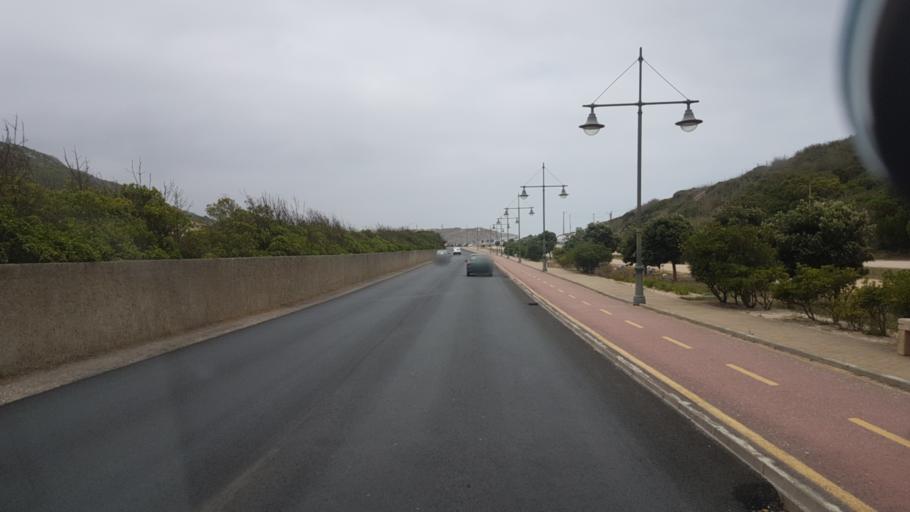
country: PT
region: Lisbon
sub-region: Torres Vedras
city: A dos Cunhados
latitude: 39.1765
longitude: -9.3550
